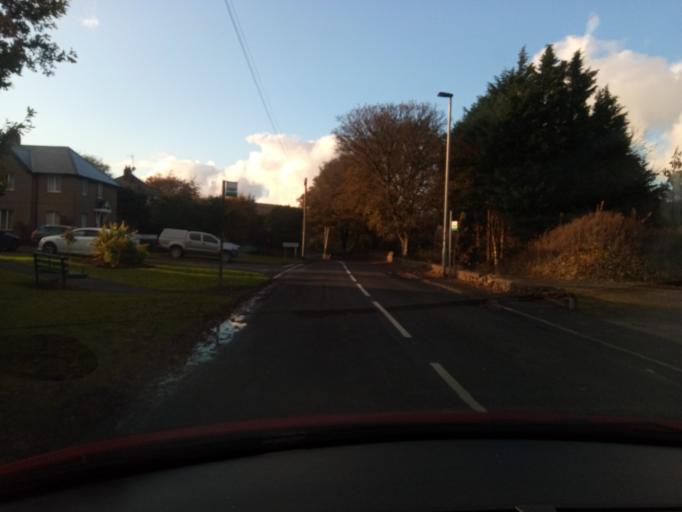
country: GB
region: England
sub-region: County Durham
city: Holwick
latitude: 54.7488
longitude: -2.2197
